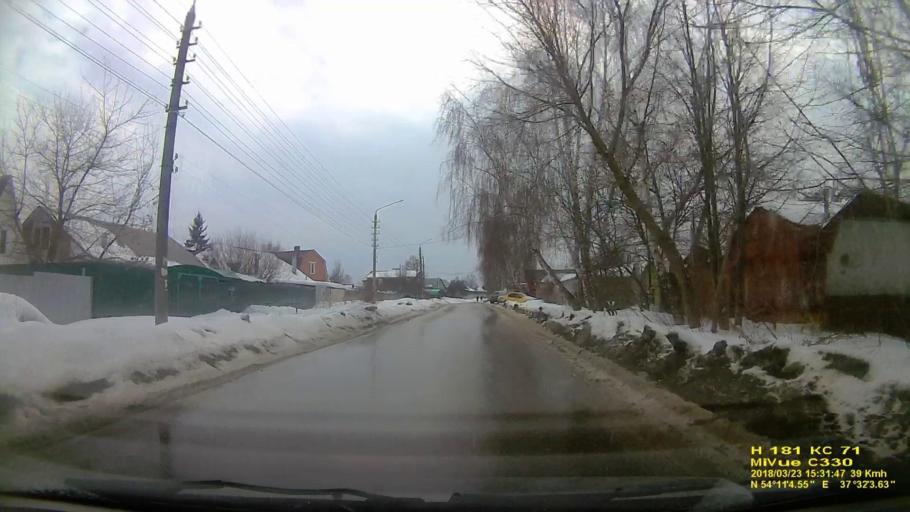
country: RU
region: Tula
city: Kosaya Gora
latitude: 54.1845
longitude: 37.5340
